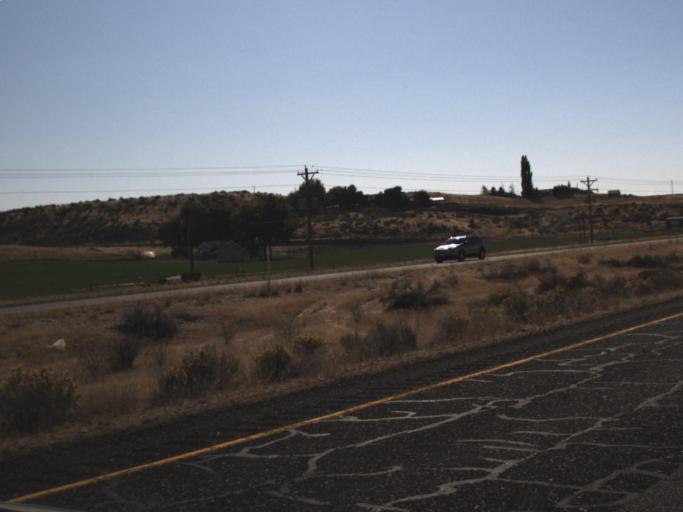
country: US
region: Washington
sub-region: Franklin County
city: Basin City
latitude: 46.4633
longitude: -119.0129
